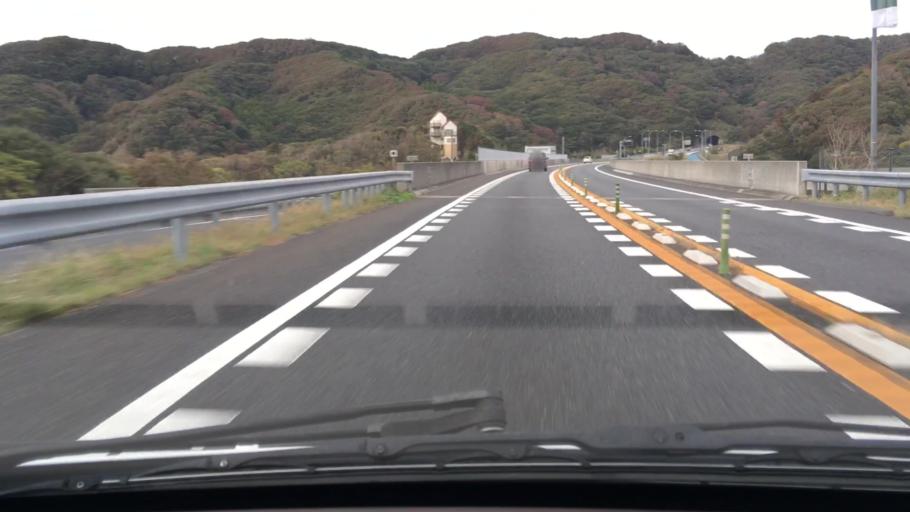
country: JP
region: Chiba
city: Futtsu
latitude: 35.1683
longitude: 139.8304
